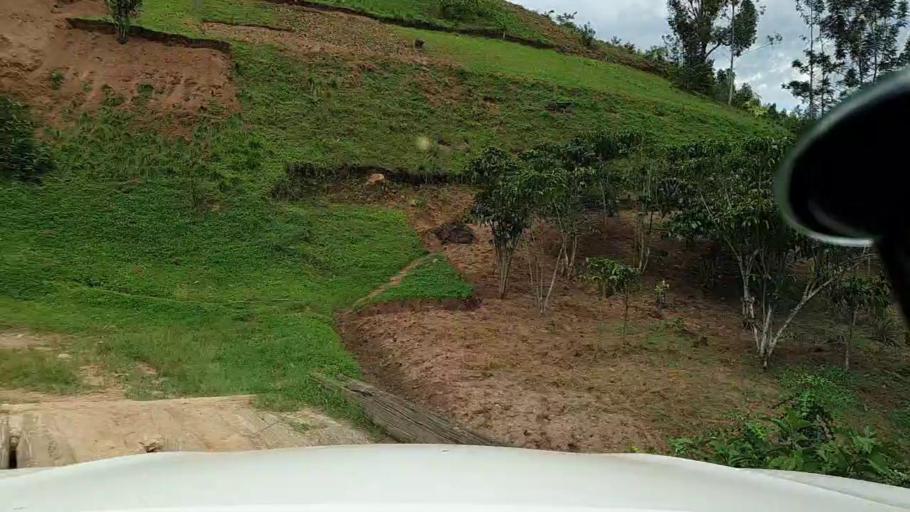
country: RW
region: Southern Province
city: Gitarama
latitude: -1.8141
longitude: 29.8021
